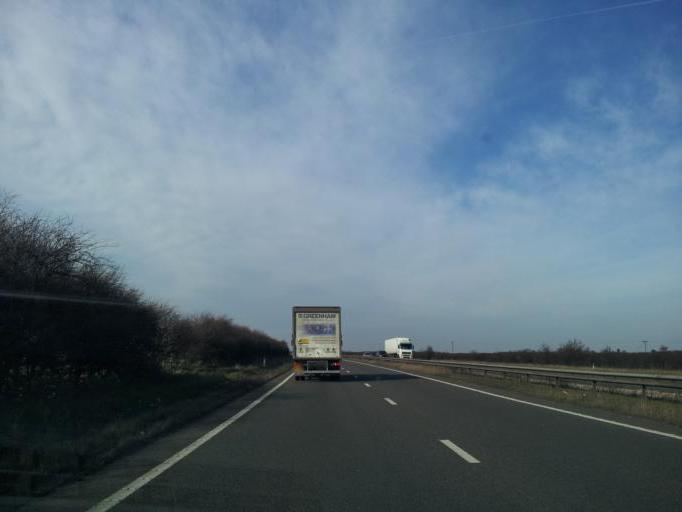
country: GB
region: England
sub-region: Lincolnshire
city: Long Bennington
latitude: 53.0325
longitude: -0.7718
